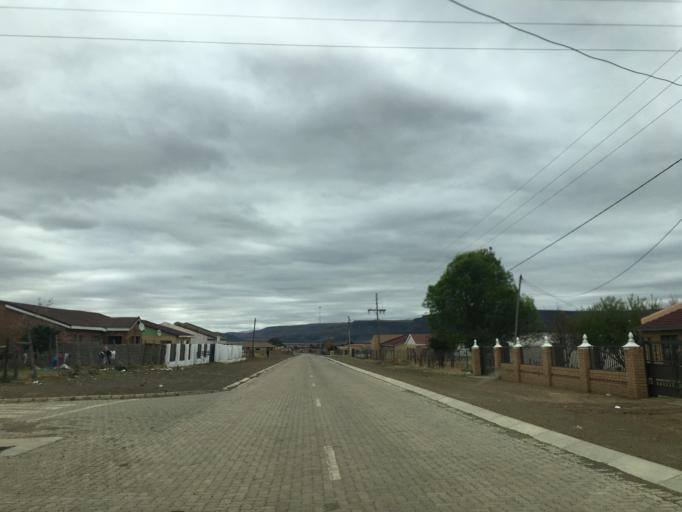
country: ZA
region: Eastern Cape
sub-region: Chris Hani District Municipality
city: Cala
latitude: -31.5374
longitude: 27.6977
